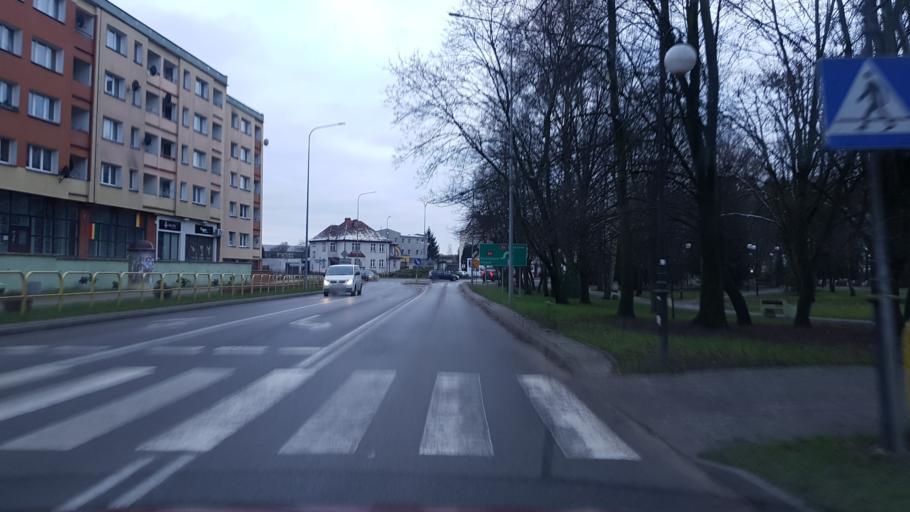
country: PL
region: Pomeranian Voivodeship
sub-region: Powiat bytowski
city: Miastko
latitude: 54.0001
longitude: 16.9757
